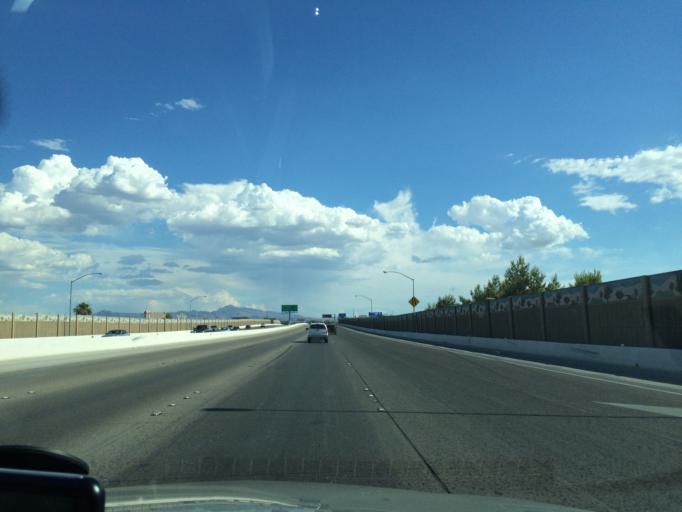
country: US
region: Nevada
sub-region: Clark County
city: Winchester
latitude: 36.1504
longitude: -115.0915
